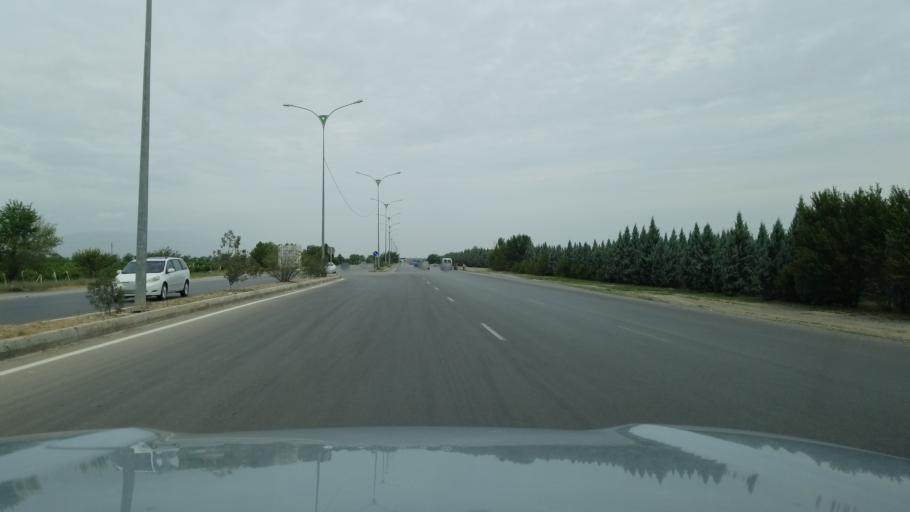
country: TM
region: Ahal
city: Abadan
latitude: 38.0907
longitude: 58.1054
